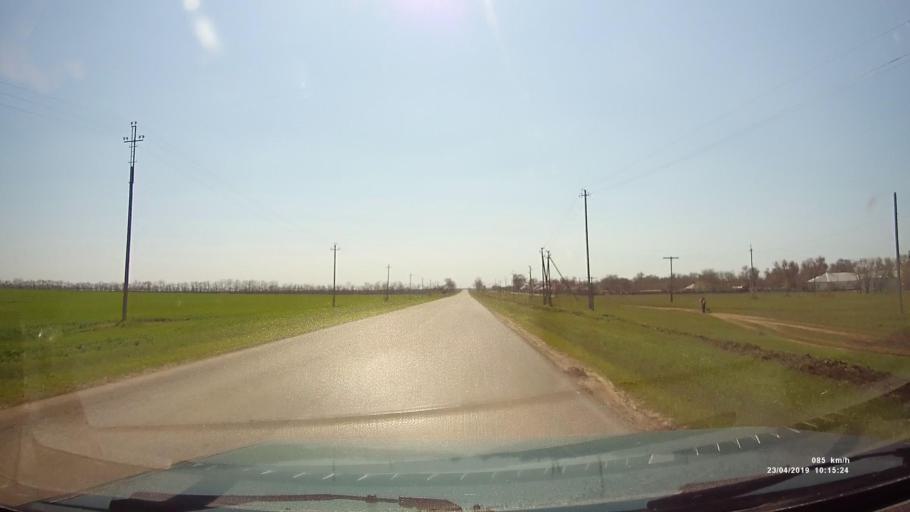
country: RU
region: Rostov
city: Sovetskoye
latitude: 46.6677
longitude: 42.3810
